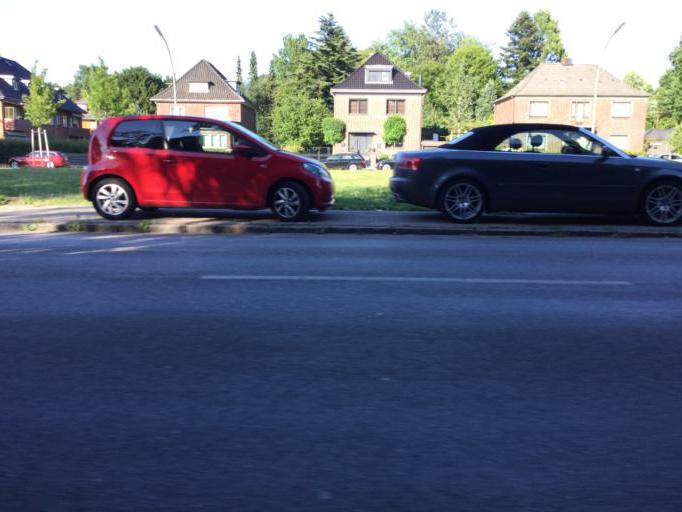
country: DE
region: Hamburg
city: Alsterdorf
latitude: 53.6112
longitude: 10.0101
